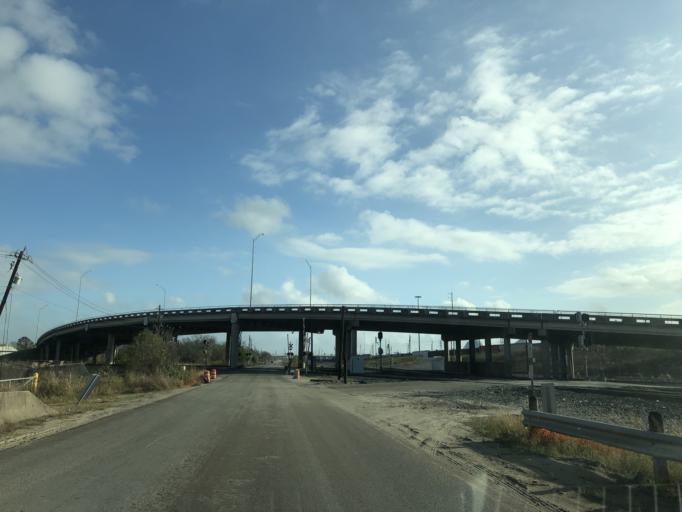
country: US
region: Texas
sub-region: Harris County
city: Jacinto City
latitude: 29.7990
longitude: -95.2898
